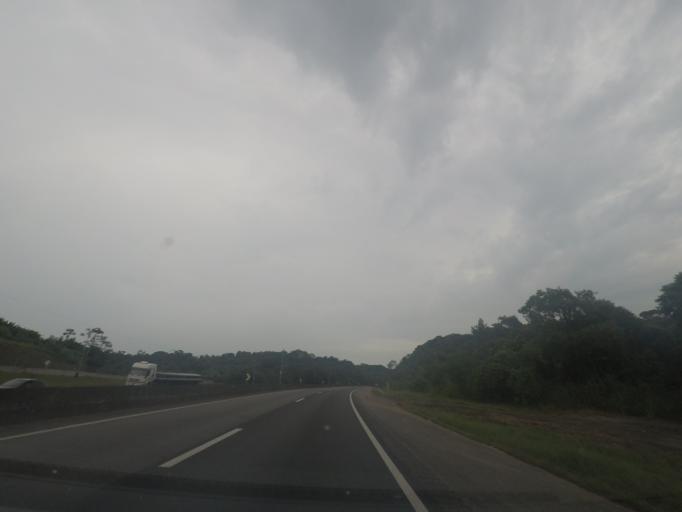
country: BR
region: Sao Paulo
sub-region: Pariquera-Acu
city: Pariquera Acu
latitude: -24.6023
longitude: -47.8765
